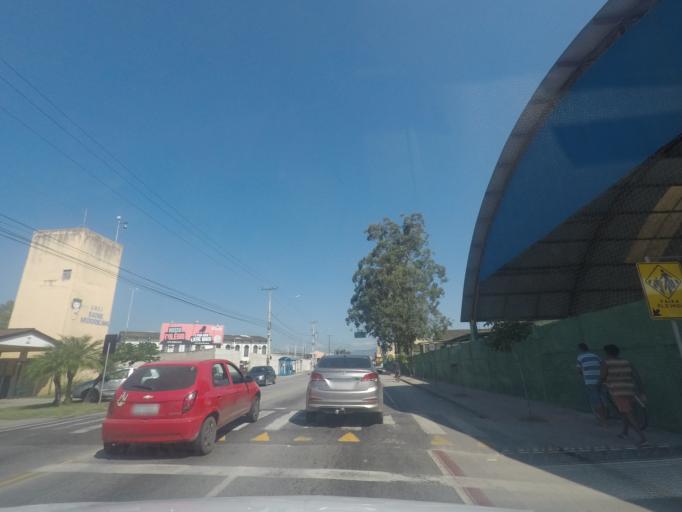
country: BR
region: Parana
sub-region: Paranagua
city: Paranagua
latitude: -25.5510
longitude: -48.5487
